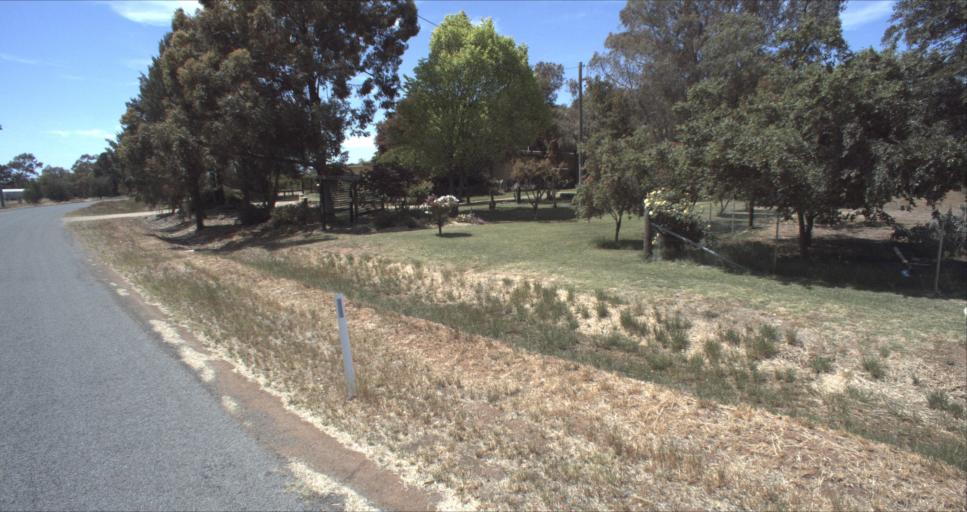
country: AU
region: New South Wales
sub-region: Leeton
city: Leeton
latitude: -34.5723
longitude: 146.4333
